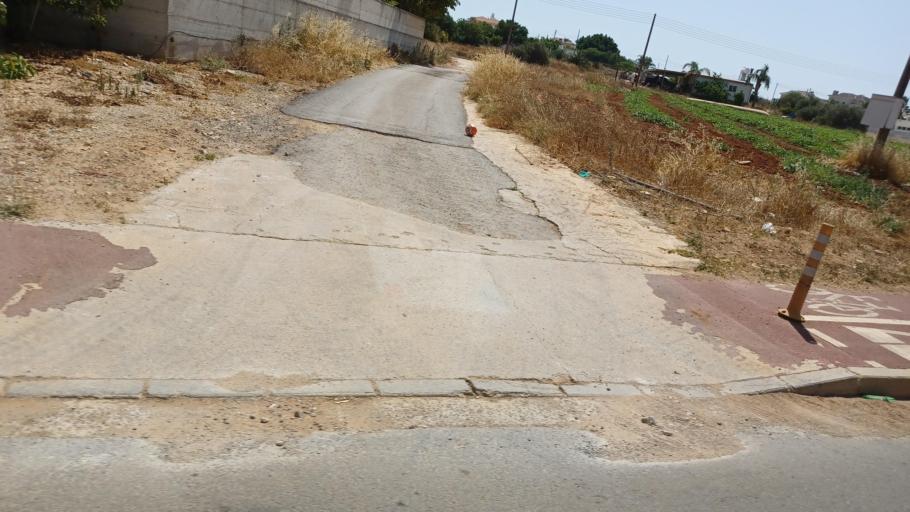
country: CY
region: Ammochostos
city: Paralimni
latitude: 35.0190
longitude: 33.9534
